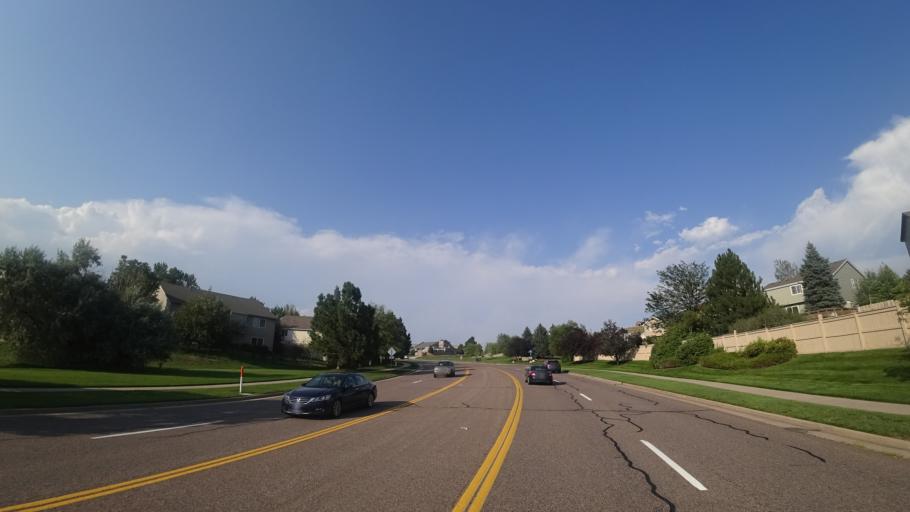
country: US
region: Colorado
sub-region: Arapahoe County
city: Dove Valley
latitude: 39.6169
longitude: -104.7401
